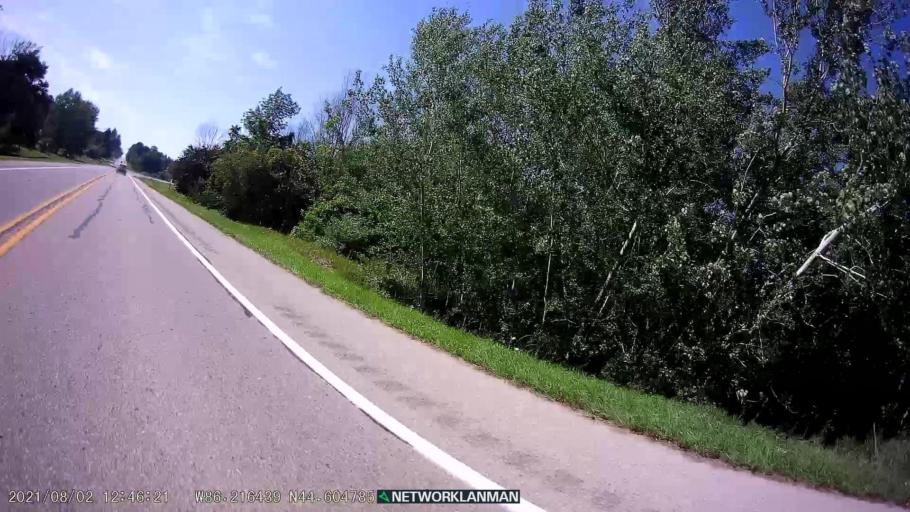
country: US
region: Michigan
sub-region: Benzie County
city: Frankfort
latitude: 44.6049
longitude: -86.2172
